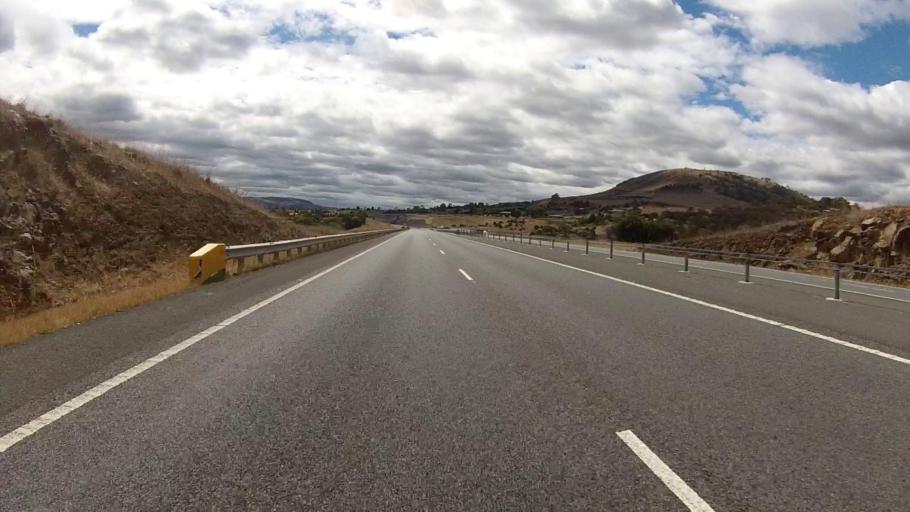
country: AU
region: Tasmania
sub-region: Brighton
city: Bridgewater
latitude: -42.7059
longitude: 147.2622
